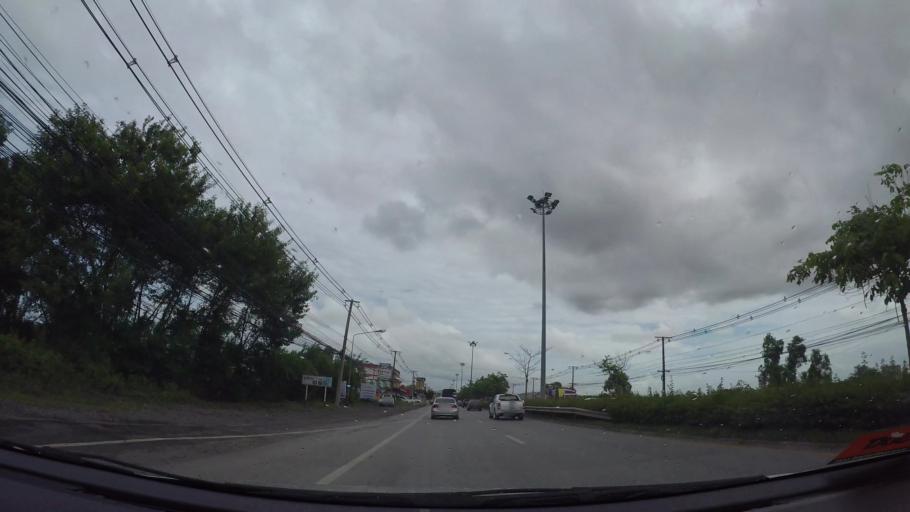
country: TH
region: Rayong
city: Rayong
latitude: 12.6972
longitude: 101.1953
